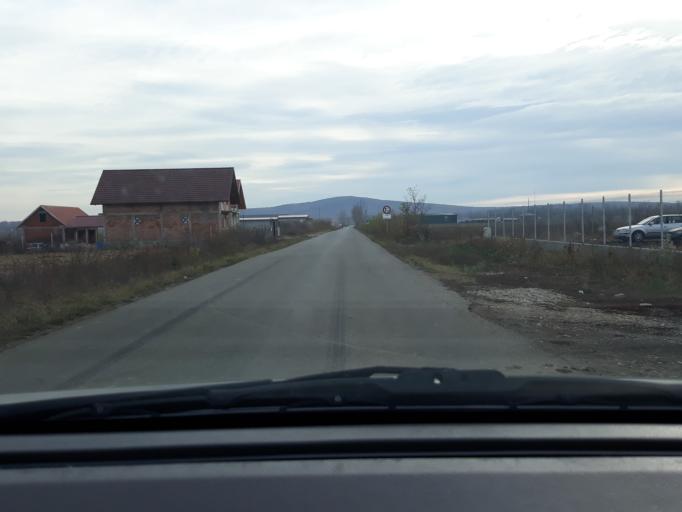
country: RO
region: Bihor
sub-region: Comuna Sanmartin
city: Sanmartin
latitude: 47.0280
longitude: 22.0024
